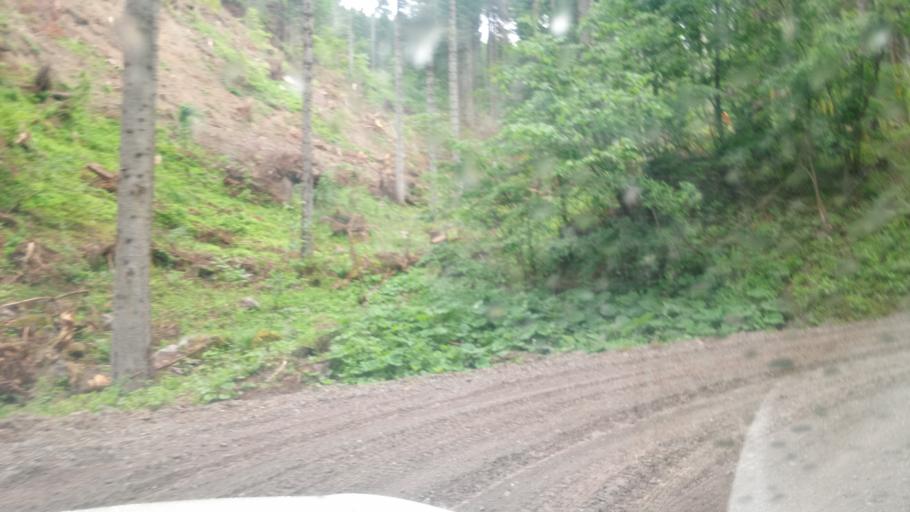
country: IT
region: Friuli Venezia Giulia
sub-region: Provincia di Udine
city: Paluzza
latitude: 46.5684
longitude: 13.0167
